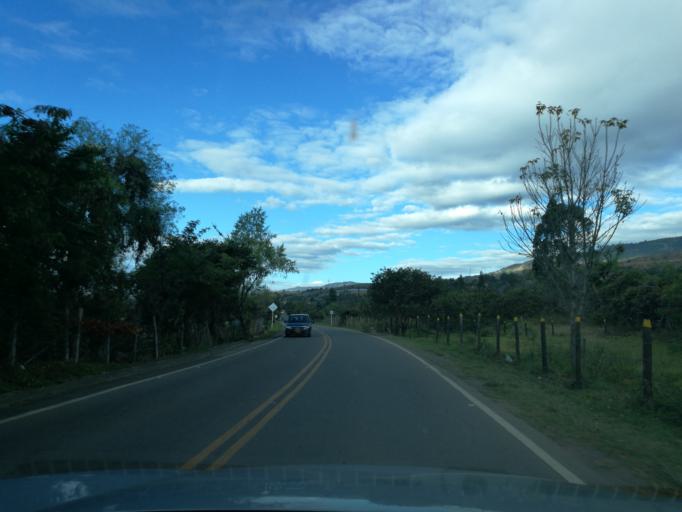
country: CO
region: Boyaca
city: Sutamarchan
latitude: 5.6115
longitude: -73.6286
